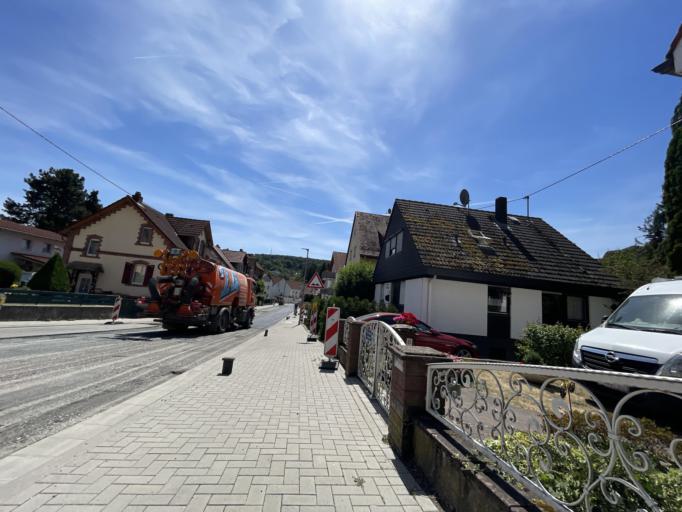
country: GB
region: England
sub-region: East Sussex
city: Eastbourne
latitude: 50.5904
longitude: 0.4552
